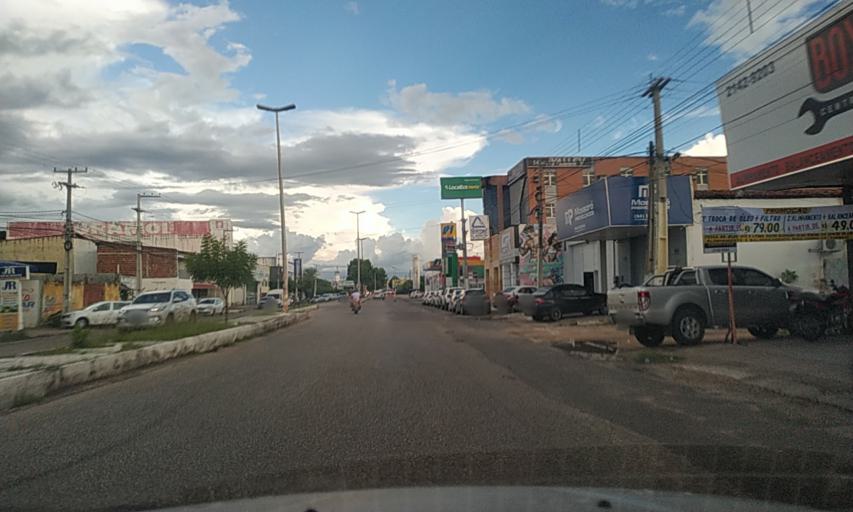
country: BR
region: Rio Grande do Norte
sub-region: Mossoro
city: Mossoro
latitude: -5.1985
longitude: -37.3403
